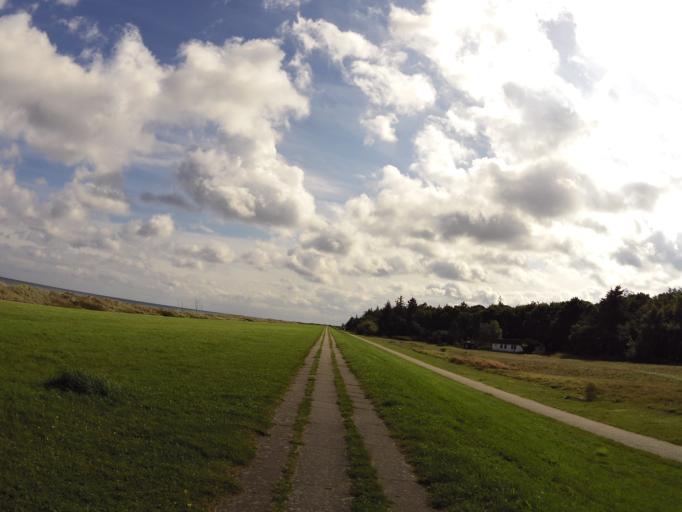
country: DE
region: Schleswig-Holstein
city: Wisch
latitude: 54.4346
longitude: 10.3318
